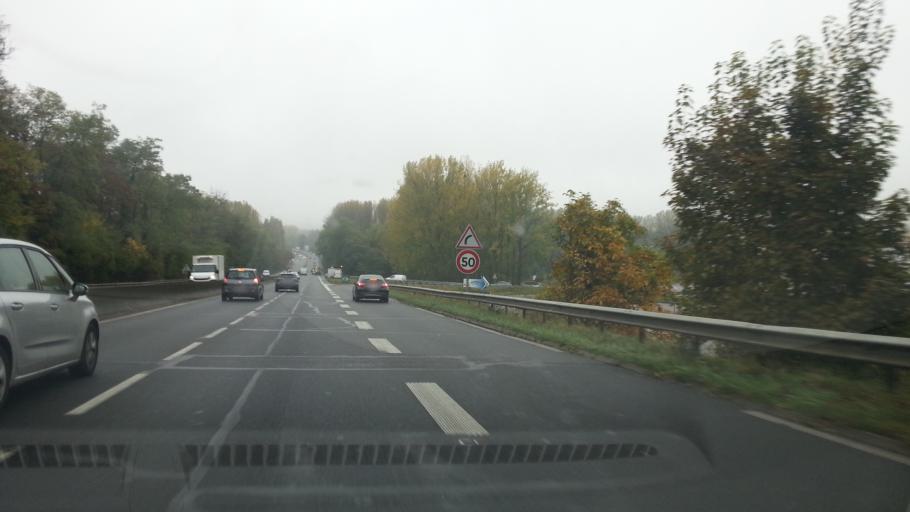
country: FR
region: Picardie
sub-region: Departement de l'Oise
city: Cauffry
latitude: 49.3206
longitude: 2.4396
